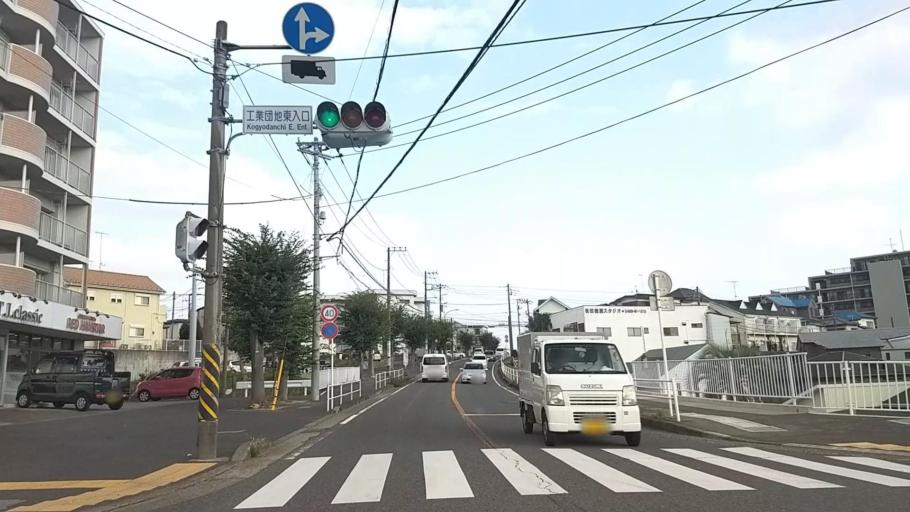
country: JP
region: Kanagawa
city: Isehara
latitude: 35.3934
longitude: 139.3032
